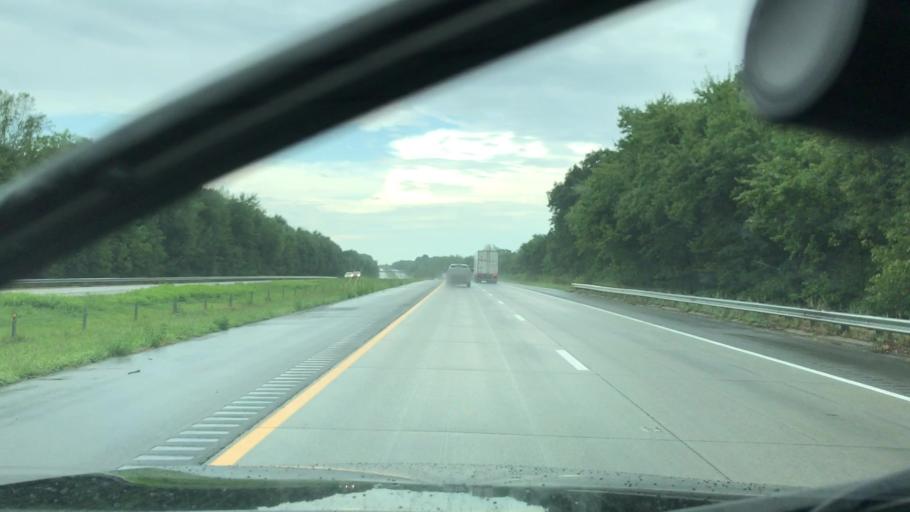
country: US
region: North Carolina
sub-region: Yadkin County
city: Jonesville
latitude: 36.1449
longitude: -80.8082
